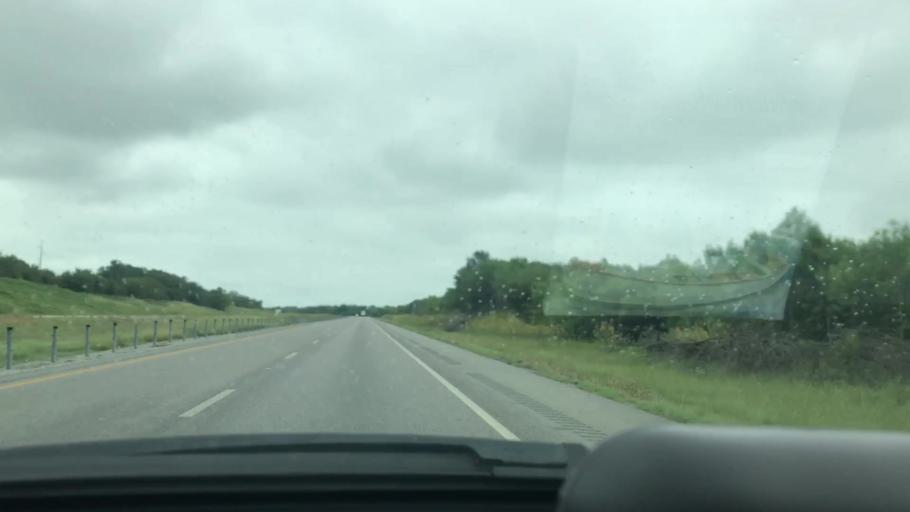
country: US
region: Oklahoma
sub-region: Coal County
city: Coalgate
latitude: 34.6420
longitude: -95.9482
